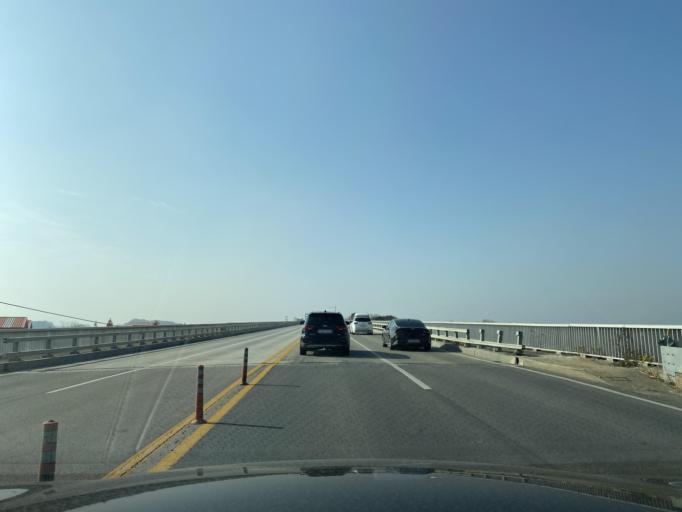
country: KR
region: Chungcheongnam-do
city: Yesan
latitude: 36.6842
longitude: 126.8053
